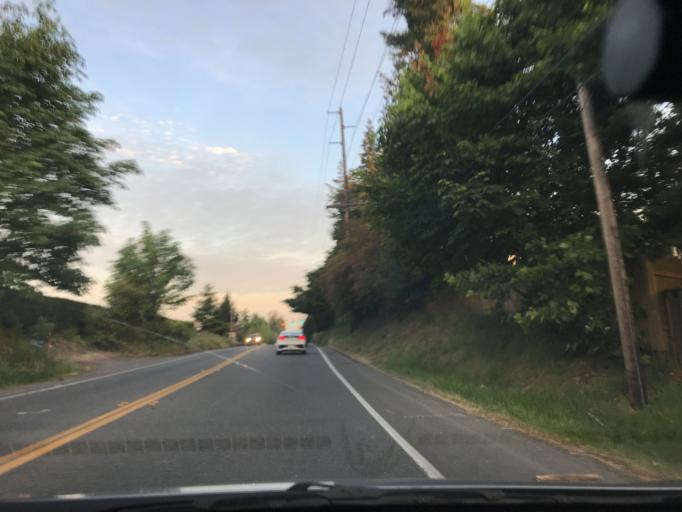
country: US
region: Washington
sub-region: King County
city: Maple Valley
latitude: 47.3580
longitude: -122.0513
